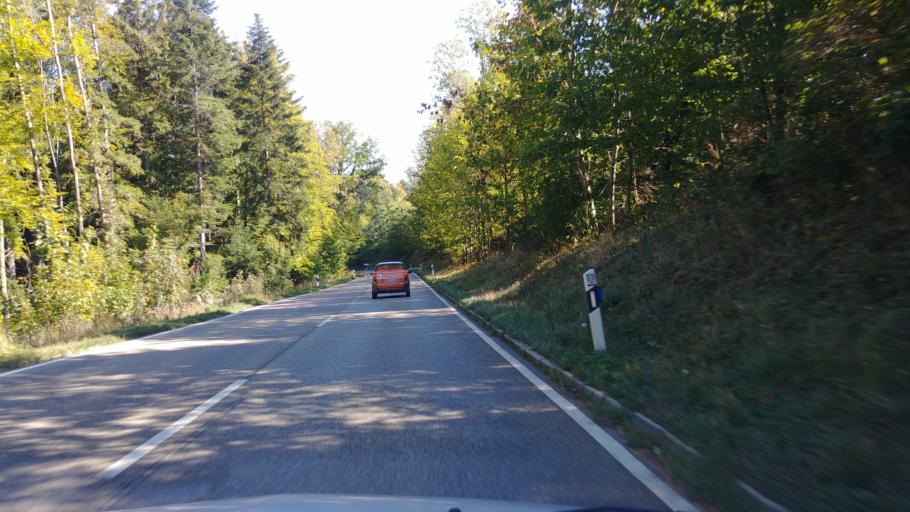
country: DE
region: Baden-Wuerttemberg
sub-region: Regierungsbezirk Stuttgart
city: Gaildorf
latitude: 48.9709
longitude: 9.7550
